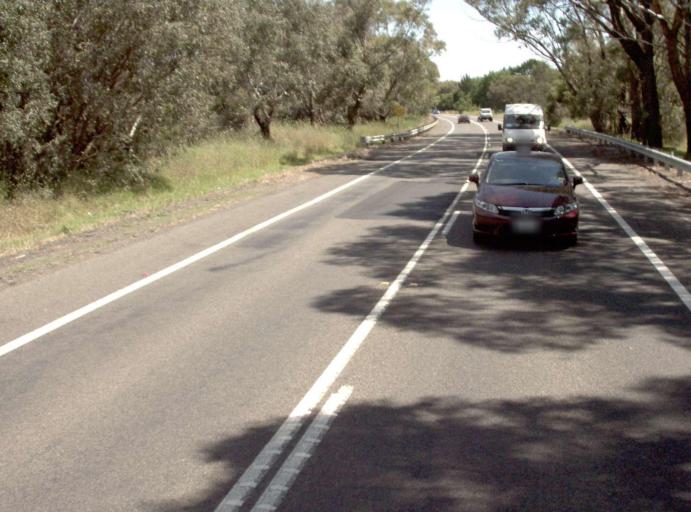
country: AU
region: Victoria
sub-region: Wellington
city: Sale
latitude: -37.9869
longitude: 147.0680
